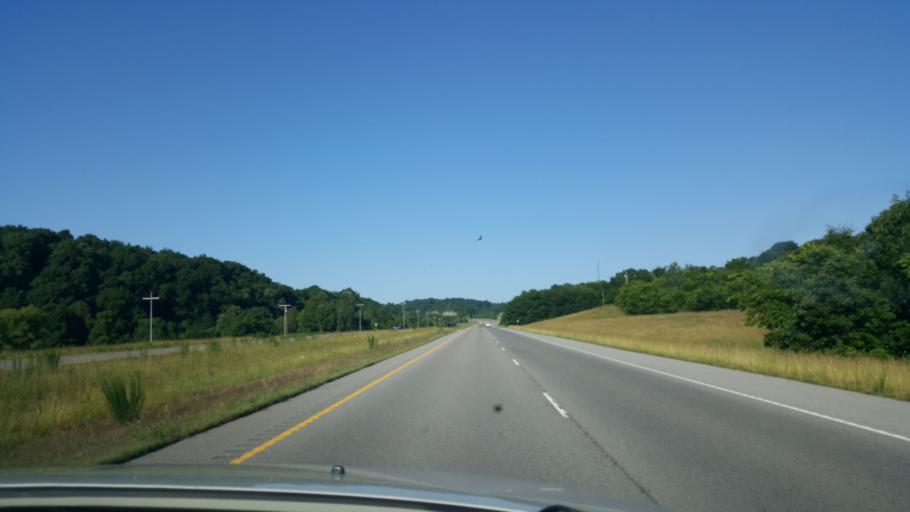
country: US
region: Tennessee
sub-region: Maury County
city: Mount Pleasant
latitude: 35.4885
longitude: -87.2424
